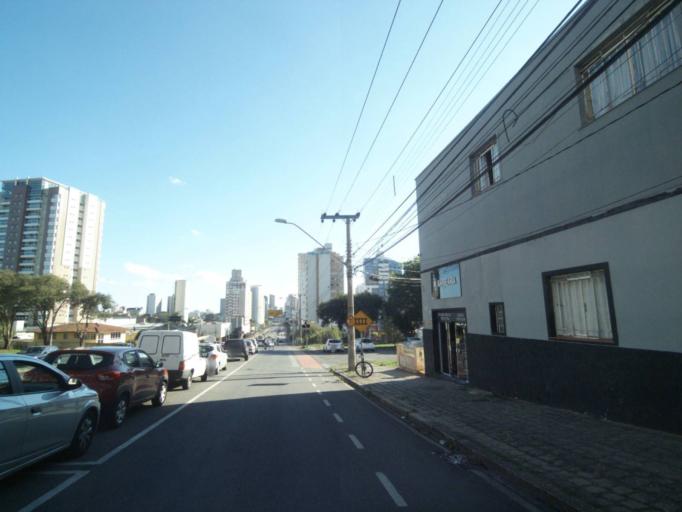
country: BR
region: Parana
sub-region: Curitiba
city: Curitiba
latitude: -25.4005
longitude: -49.2471
